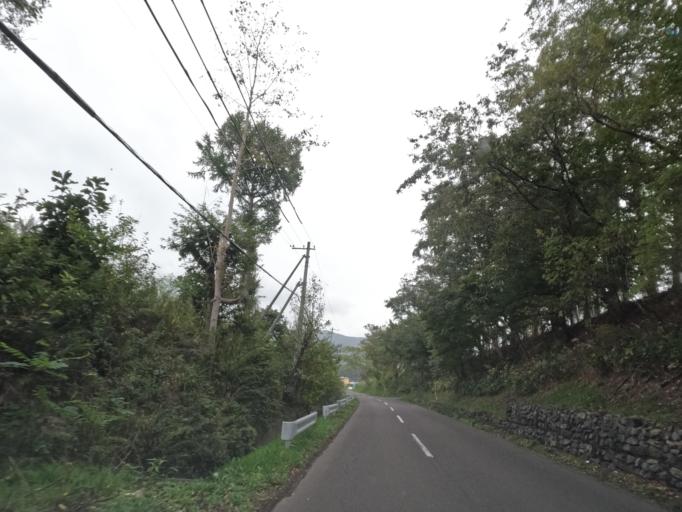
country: JP
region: Hokkaido
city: Date
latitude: 42.4744
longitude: 140.8910
